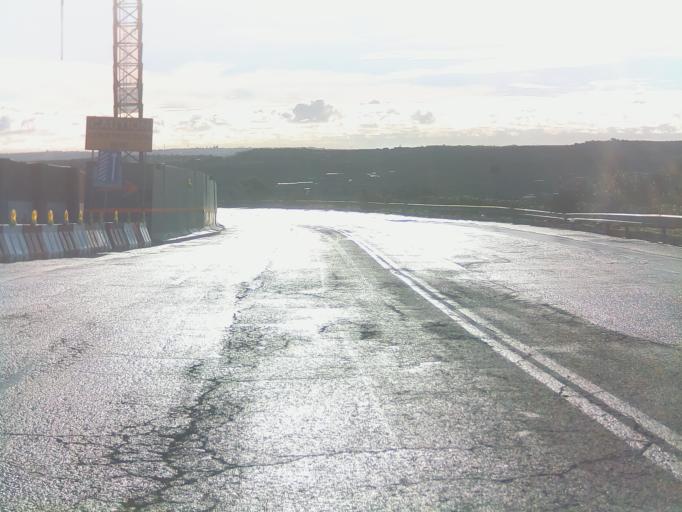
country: MT
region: Il-Mellieha
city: Mellieha
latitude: 35.9532
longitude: 14.3643
